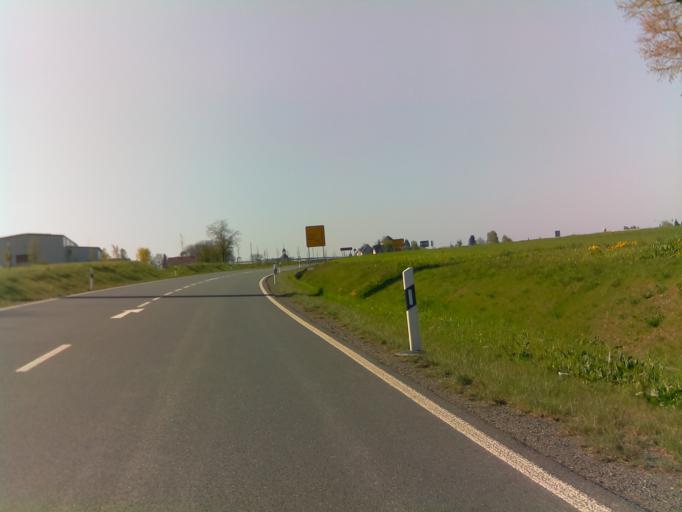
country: DE
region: Thuringia
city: Dittersdorf
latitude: 50.6524
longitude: 11.8161
